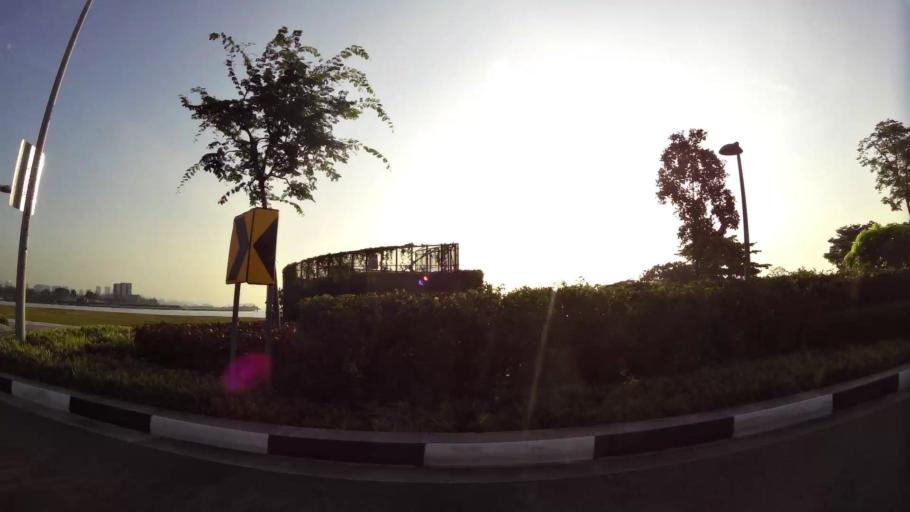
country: SG
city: Singapore
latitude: 1.2783
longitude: 103.8711
